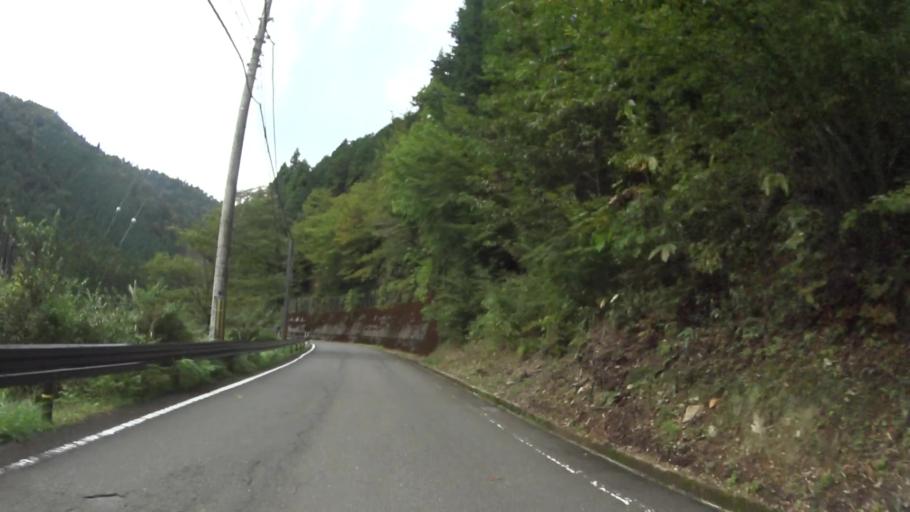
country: JP
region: Fukui
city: Obama
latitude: 35.3202
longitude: 135.6676
